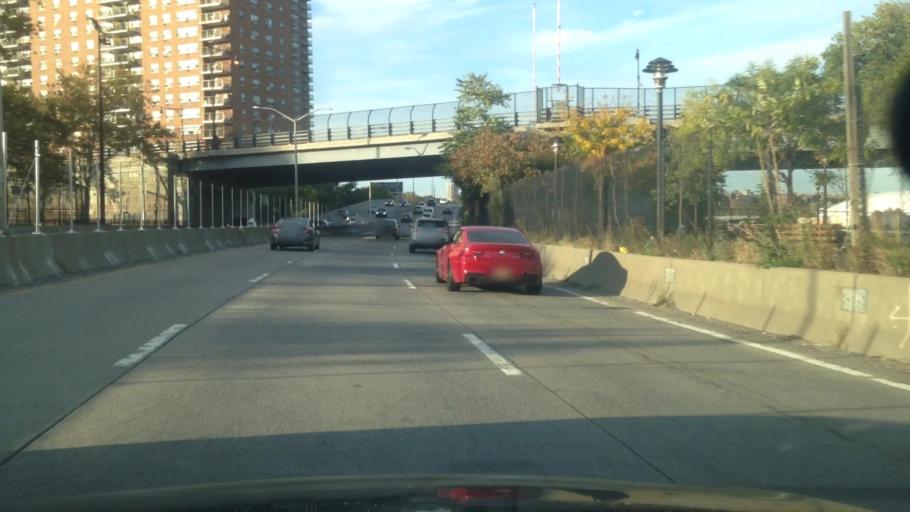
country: US
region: New Jersey
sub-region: Bergen County
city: Edgewater
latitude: 40.8189
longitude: -73.9342
